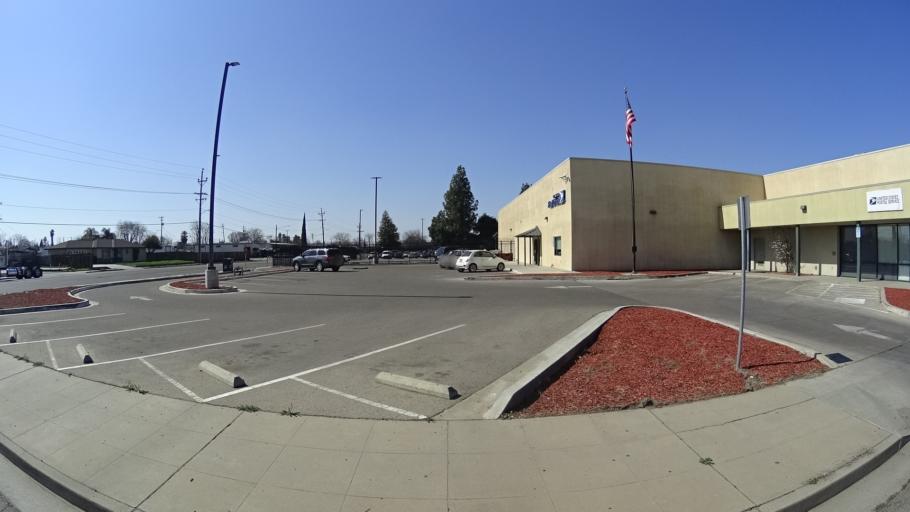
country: US
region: California
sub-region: Fresno County
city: Fresno
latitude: 36.7145
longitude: -119.7547
